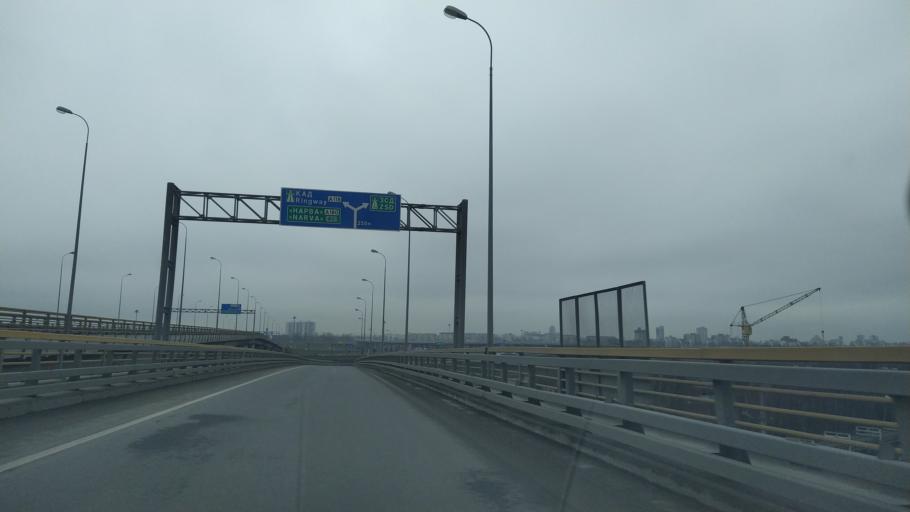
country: RU
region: St.-Petersburg
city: Dachnoye
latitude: 59.8323
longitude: 30.2907
